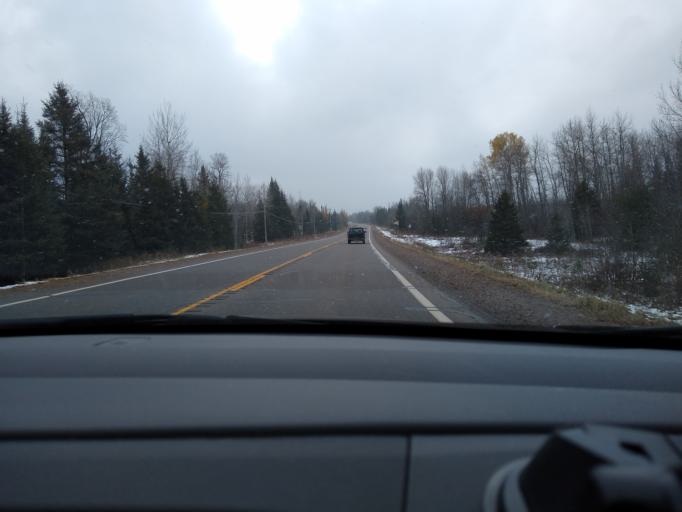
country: US
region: Michigan
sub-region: Dickinson County
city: Iron Mountain
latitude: 46.0304
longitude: -88.0599
